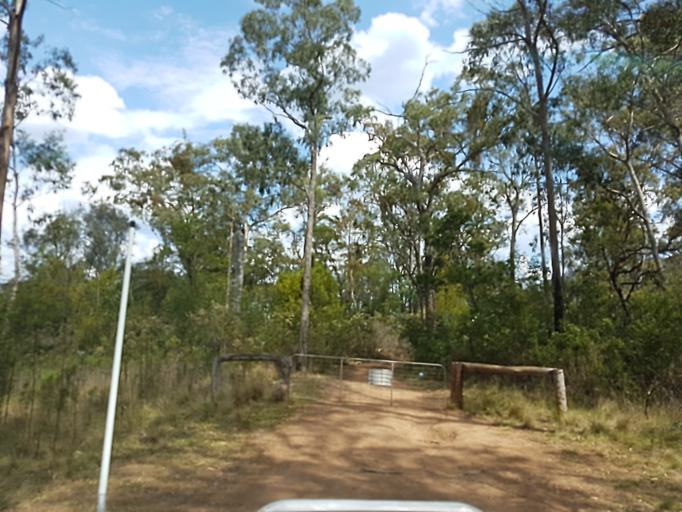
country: AU
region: Victoria
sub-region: East Gippsland
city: Lakes Entrance
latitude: -37.3987
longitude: 148.3222
